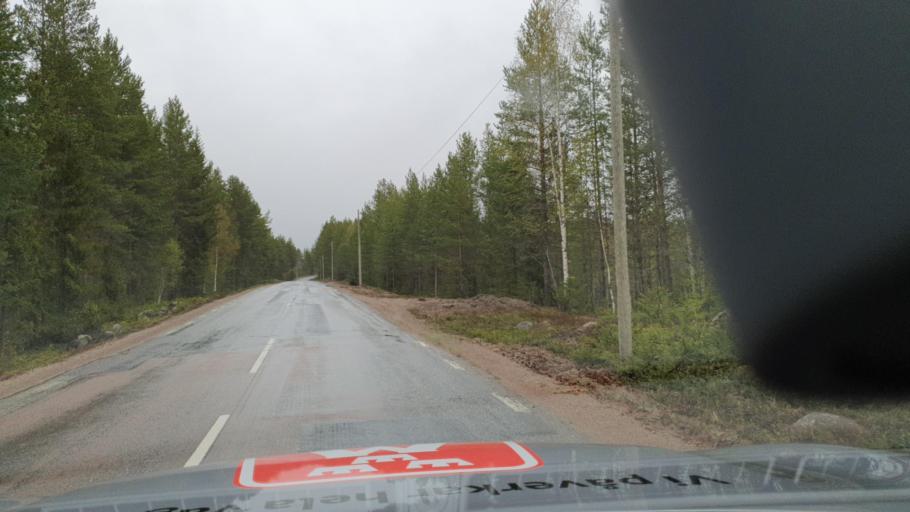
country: SE
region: Vaesternorrland
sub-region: Solleftea Kommun
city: As
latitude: 63.6758
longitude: 17.0053
